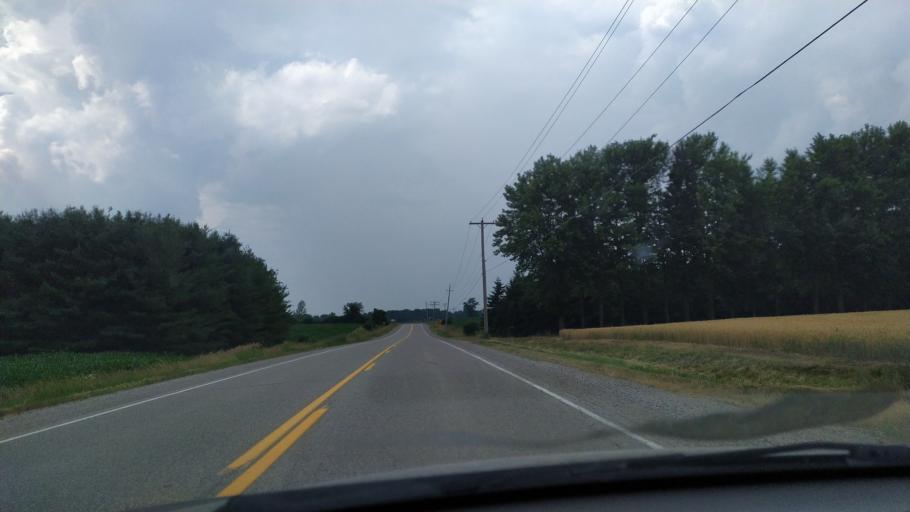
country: CA
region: Ontario
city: London
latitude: 43.2175
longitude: -81.1615
